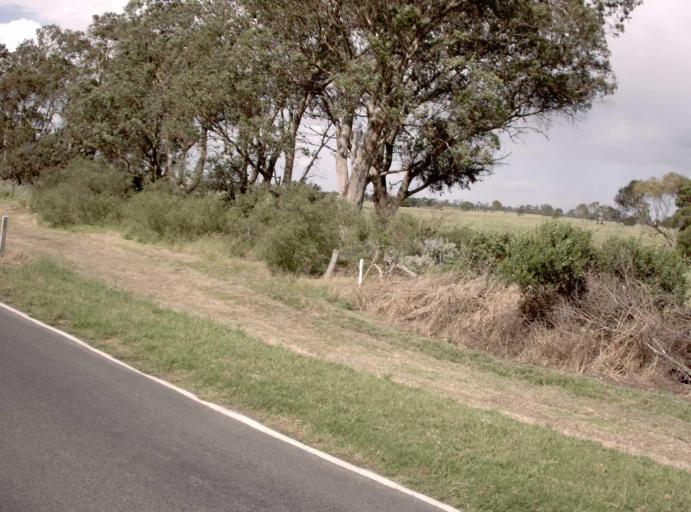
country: AU
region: Victoria
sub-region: Latrobe
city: Traralgon
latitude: -38.1506
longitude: 146.5227
